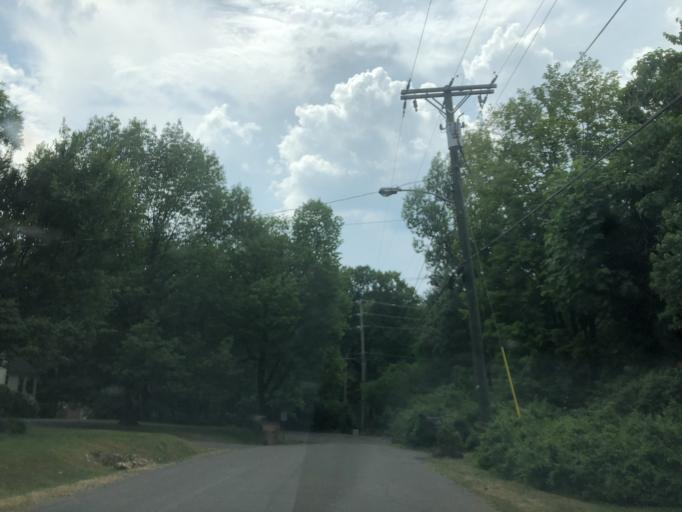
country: US
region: Tennessee
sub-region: Davidson County
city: Belle Meade
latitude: 36.1206
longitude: -86.8207
